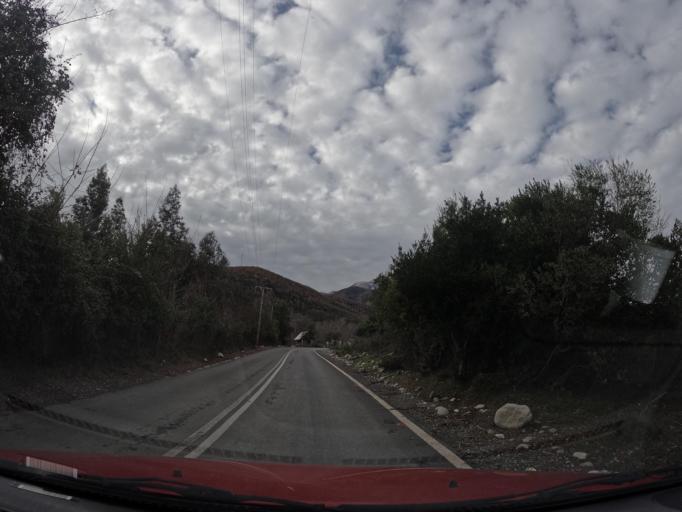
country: CL
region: Maule
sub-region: Provincia de Linares
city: Colbun
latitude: -35.8623
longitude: -71.2683
